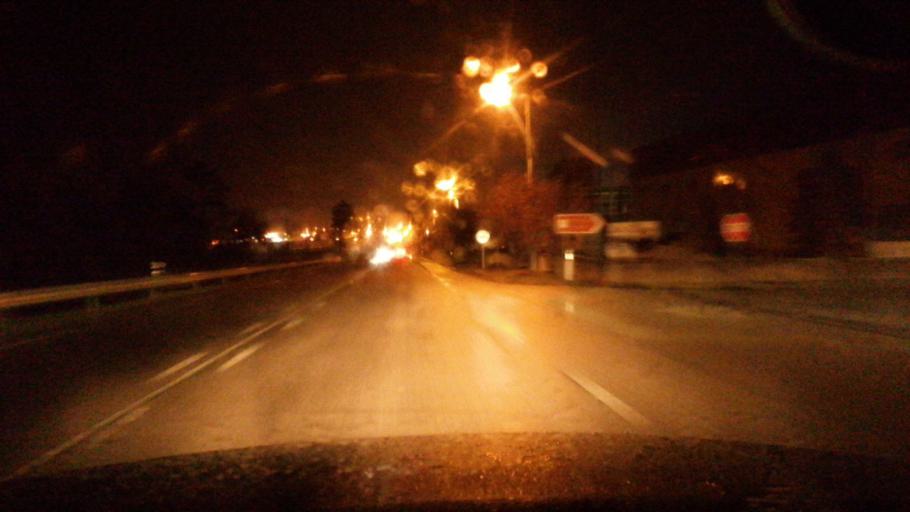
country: PT
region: Viseu
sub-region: Sernancelhe
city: Sernancelhe
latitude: 40.9013
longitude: -7.4790
